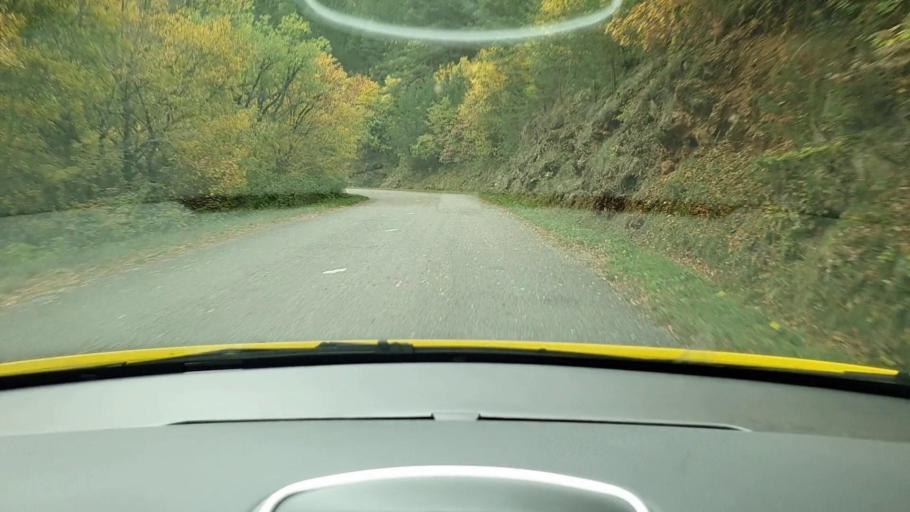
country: FR
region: Languedoc-Roussillon
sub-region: Departement de la Lozere
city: Meyrueis
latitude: 44.0758
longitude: 3.3470
